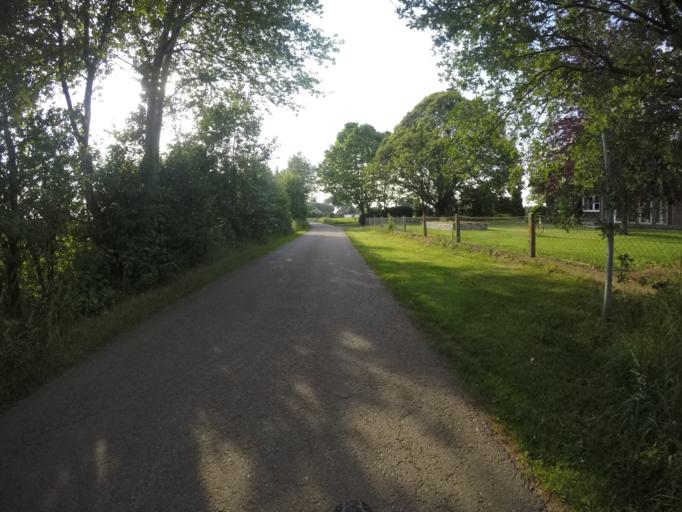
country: DE
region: North Rhine-Westphalia
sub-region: Regierungsbezirk Munster
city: Isselburg
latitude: 51.8398
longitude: 6.4807
